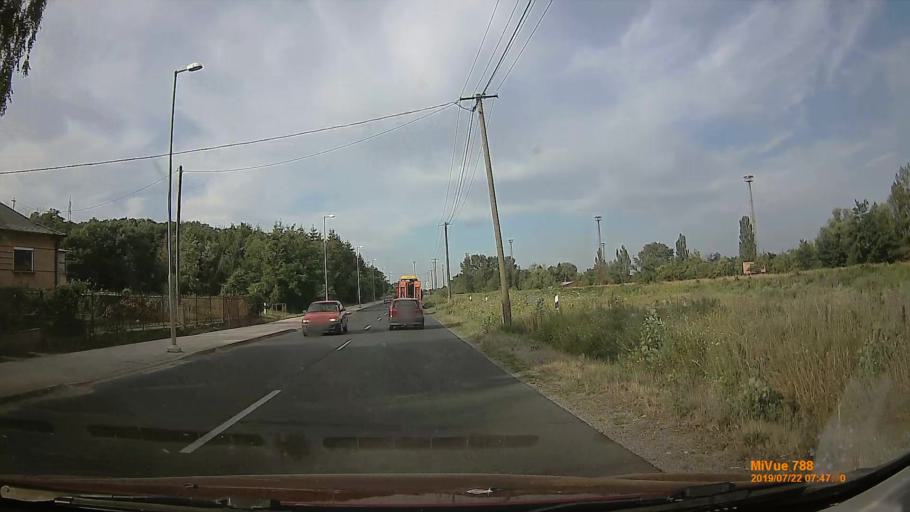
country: HU
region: Veszprem
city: Ajka
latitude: 47.0843
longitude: 17.5488
